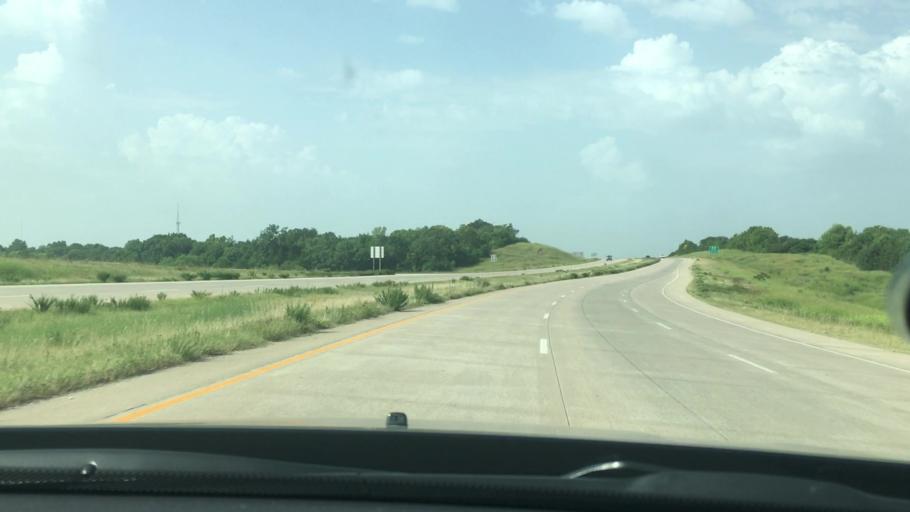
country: US
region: Oklahoma
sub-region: Pontotoc County
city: Ada
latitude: 34.7880
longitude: -96.6938
